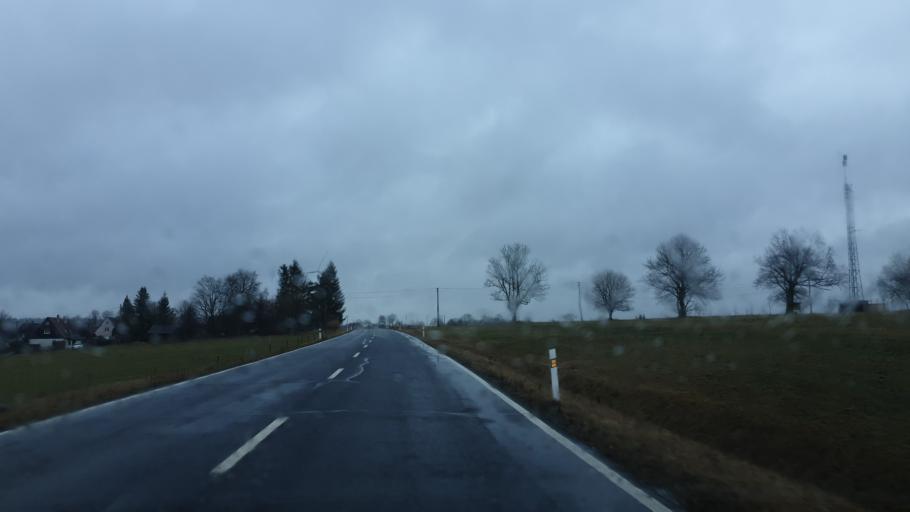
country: CZ
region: Karlovarsky
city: Hranice
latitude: 50.3059
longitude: 12.1632
